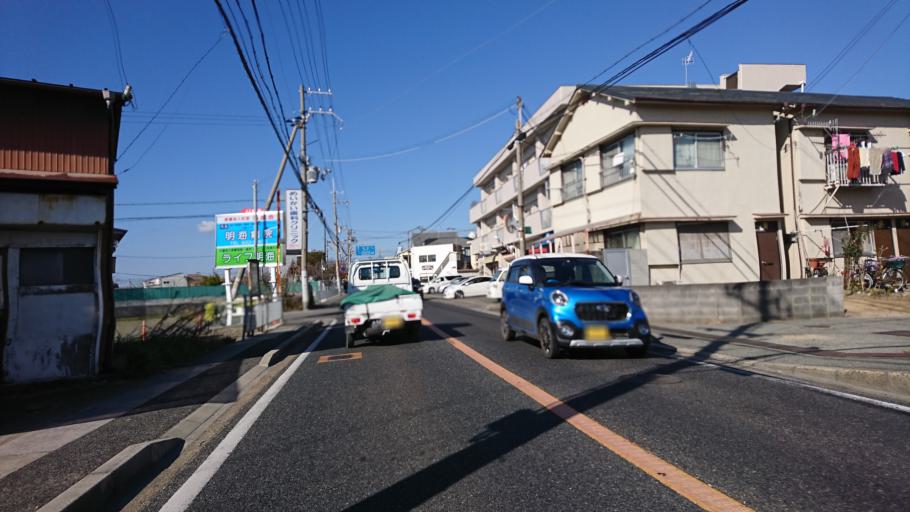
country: JP
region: Hyogo
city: Akashi
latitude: 34.6573
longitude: 134.9551
